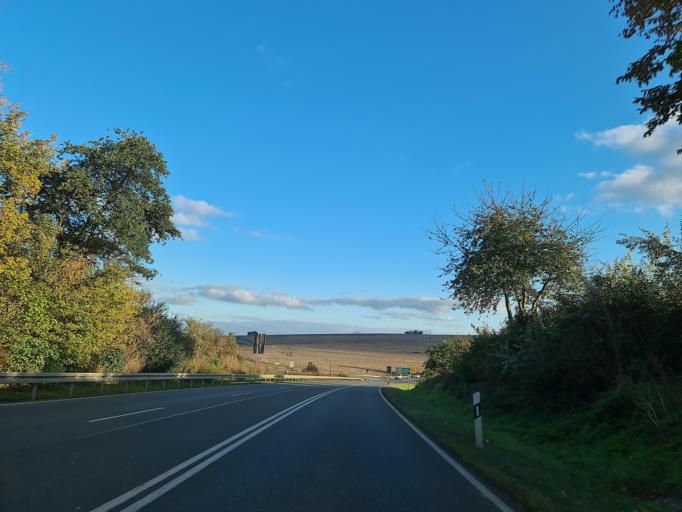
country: DE
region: Thuringia
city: Teichwitz
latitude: 50.7682
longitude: 12.0860
